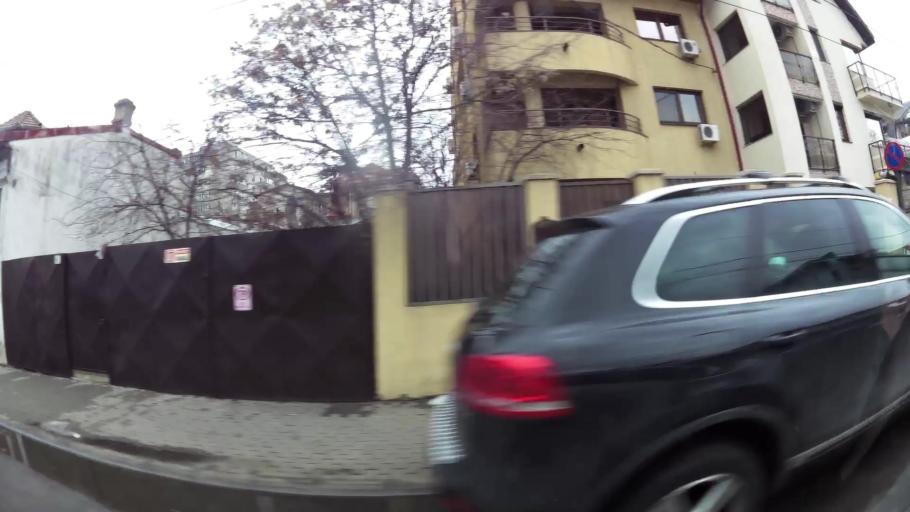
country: RO
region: Bucuresti
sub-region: Municipiul Bucuresti
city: Bucuresti
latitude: 44.4584
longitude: 26.0709
